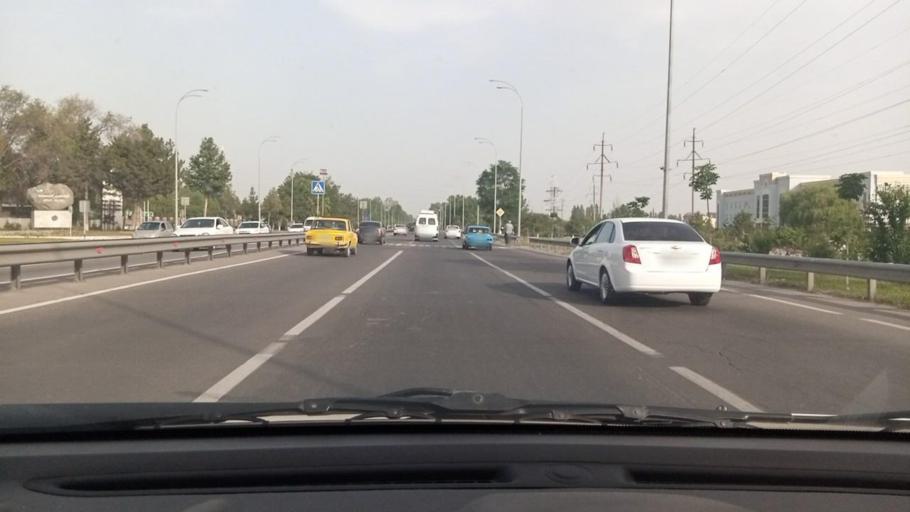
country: UZ
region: Toshkent Shahri
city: Bektemir
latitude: 41.2560
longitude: 69.3815
